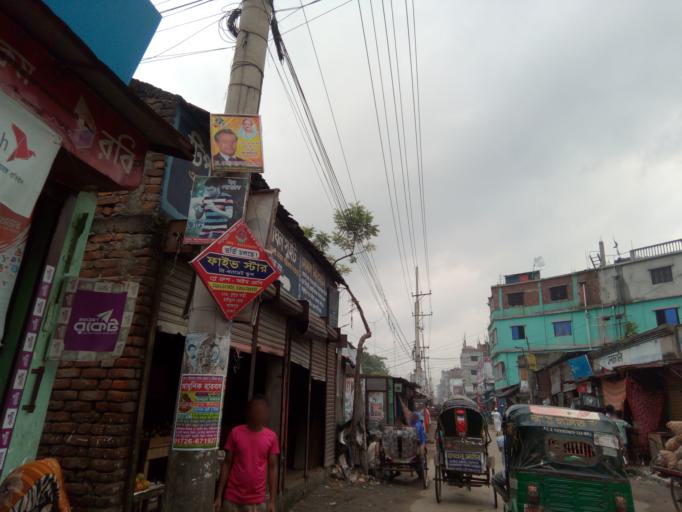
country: BD
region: Dhaka
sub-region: Dhaka
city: Dhaka
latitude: 23.6869
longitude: 90.4409
